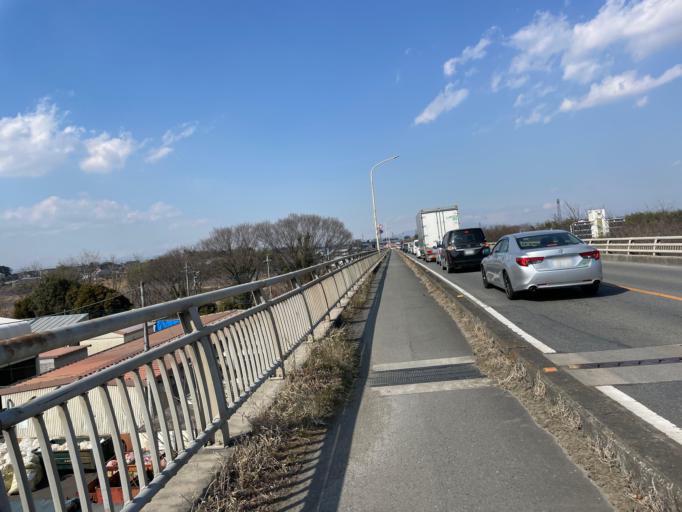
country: JP
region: Saitama
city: Yorii
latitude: 36.1160
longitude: 139.2429
